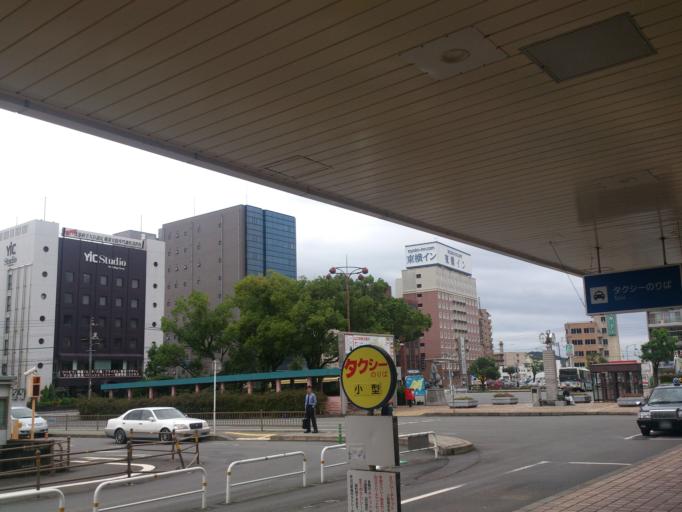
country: JP
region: Yamaguchi
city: Ogori-shimogo
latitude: 34.0925
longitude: 131.3978
